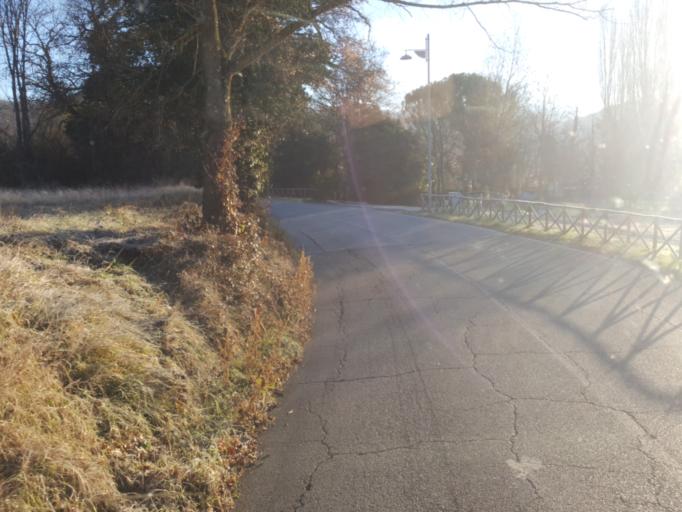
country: IT
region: Latium
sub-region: Provincia di Rieti
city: Labro
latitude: 42.5349
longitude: 12.7649
